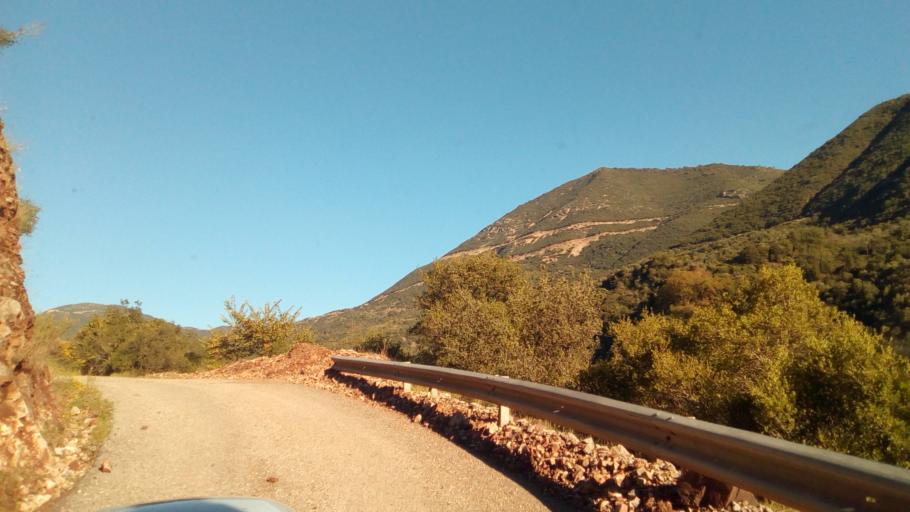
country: GR
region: West Greece
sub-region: Nomos Aitolias kai Akarnanias
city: Nafpaktos
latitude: 38.4664
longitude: 21.8735
